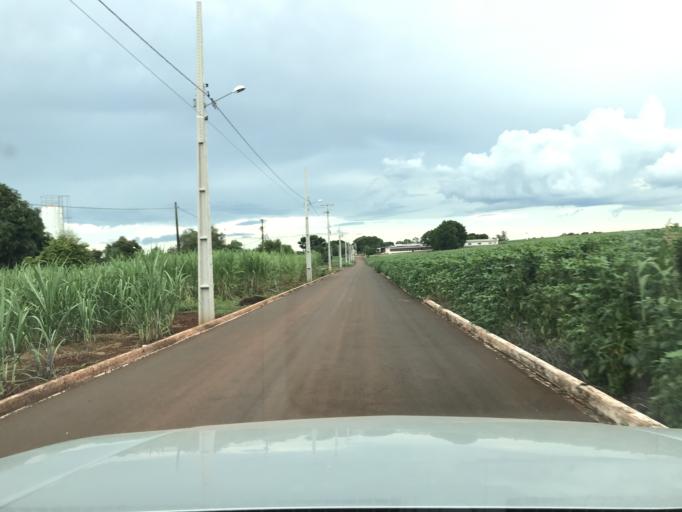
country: BR
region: Parana
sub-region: Palotina
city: Palotina
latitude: -24.2815
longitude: -53.7930
